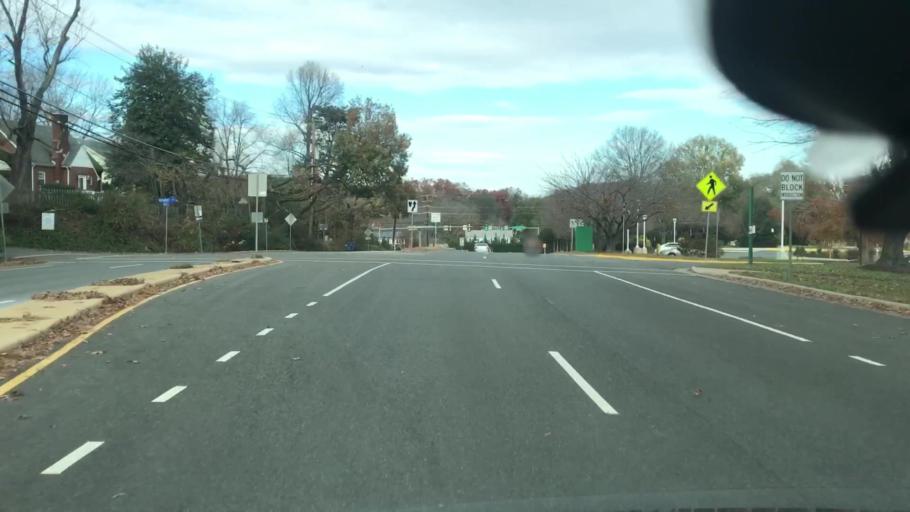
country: US
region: Virginia
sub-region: Fairfax County
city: Mantua
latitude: 38.8352
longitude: -77.2391
